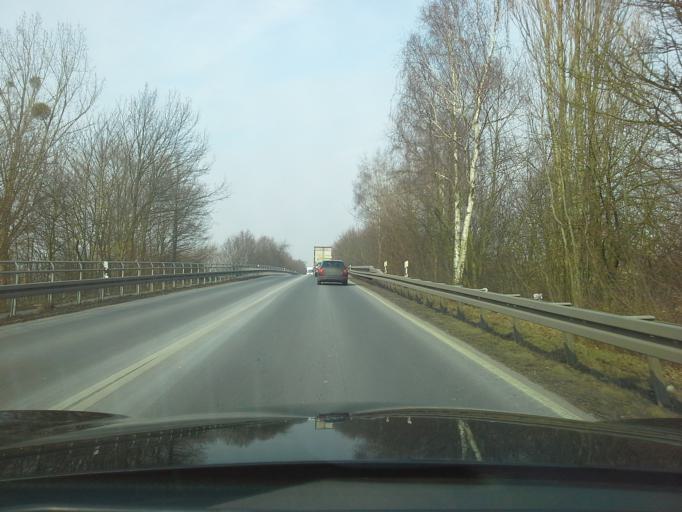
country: DE
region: Lower Saxony
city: Gross Munzel
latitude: 52.3992
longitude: 9.4642
